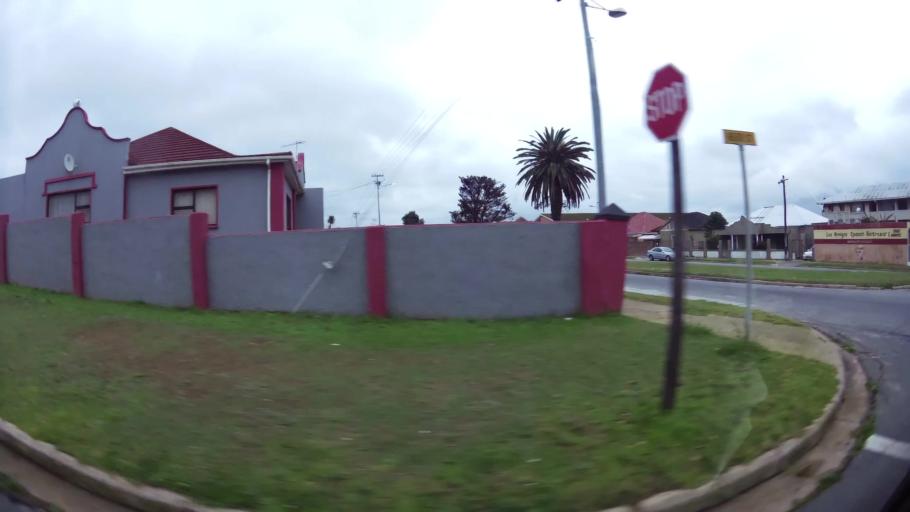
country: ZA
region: Eastern Cape
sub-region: Nelson Mandela Bay Metropolitan Municipality
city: Port Elizabeth
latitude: -33.9297
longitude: 25.5996
